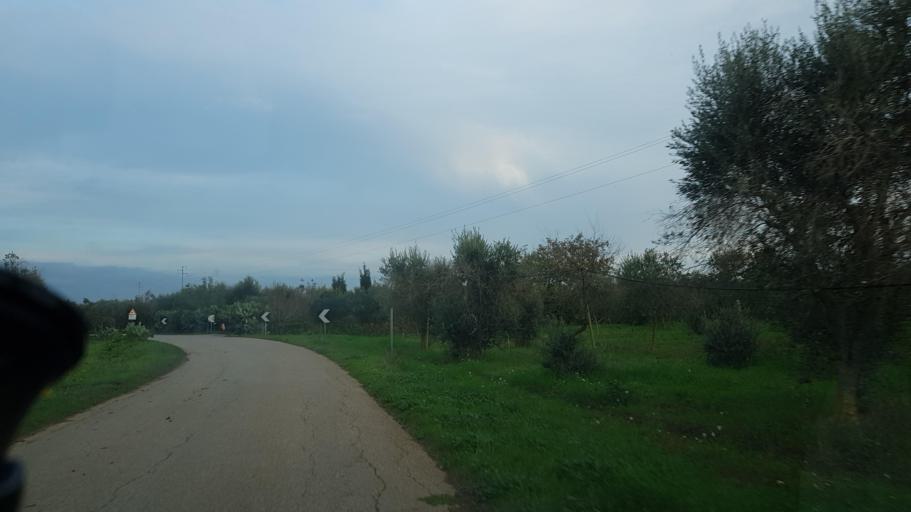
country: IT
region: Apulia
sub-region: Provincia di Brindisi
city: Latiano
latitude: 40.5382
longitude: 17.7500
